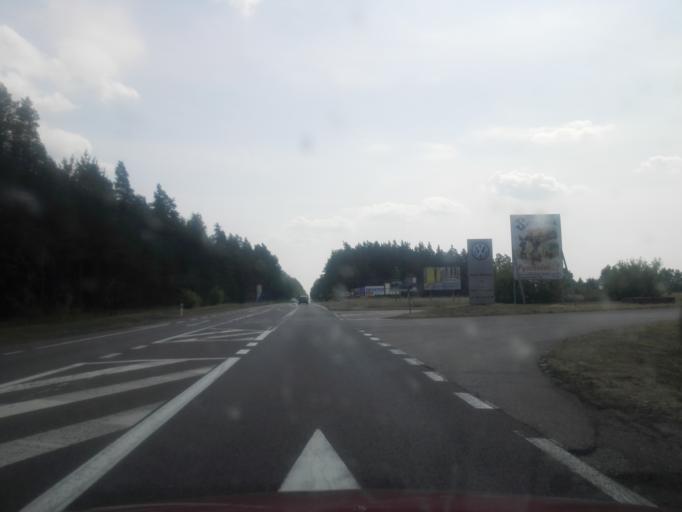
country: PL
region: Podlasie
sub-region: Suwalki
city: Suwalki
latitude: 54.0526
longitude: 22.9369
